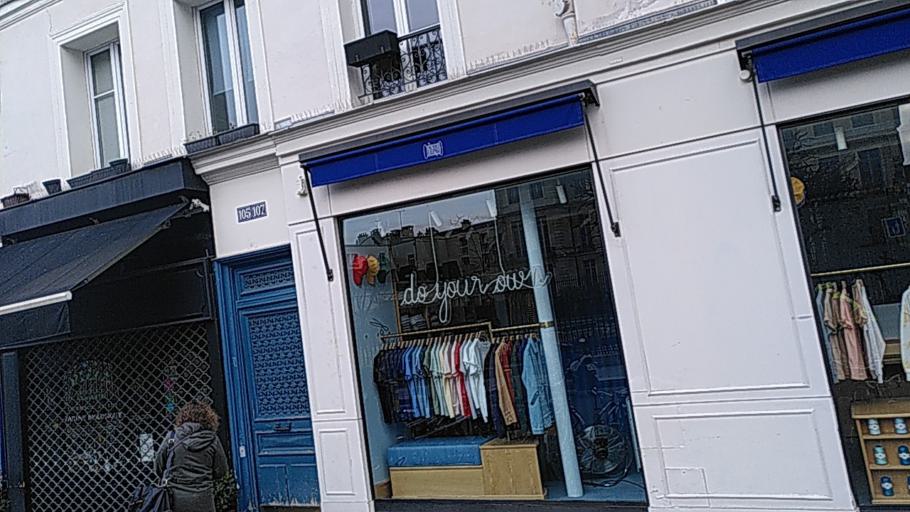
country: FR
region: Ile-de-France
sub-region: Paris
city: Paris
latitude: 48.8606
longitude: 2.3618
